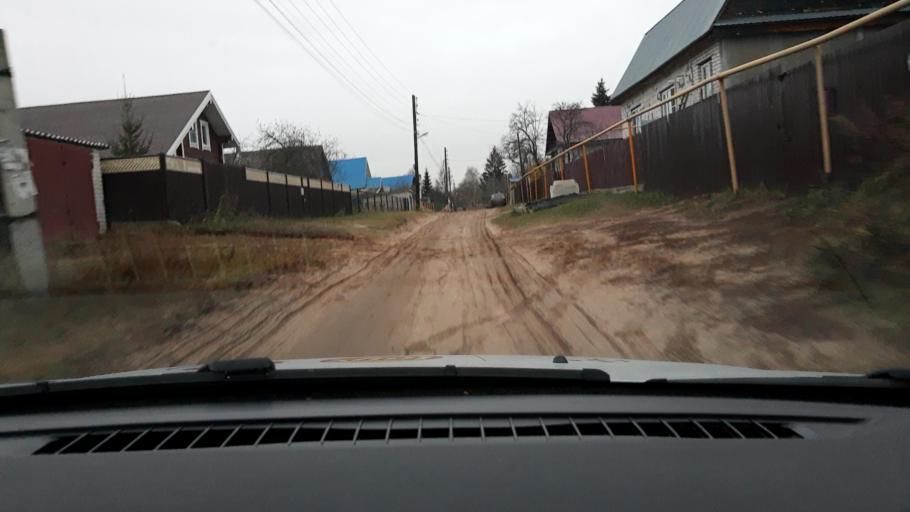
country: RU
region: Nizjnij Novgorod
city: Neklyudovo
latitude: 56.4207
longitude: 44.0203
